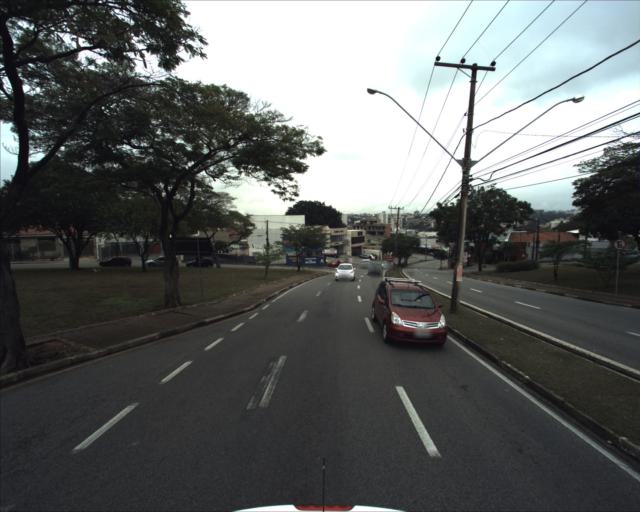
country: BR
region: Sao Paulo
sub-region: Sorocaba
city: Sorocaba
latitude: -23.5181
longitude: -47.4708
